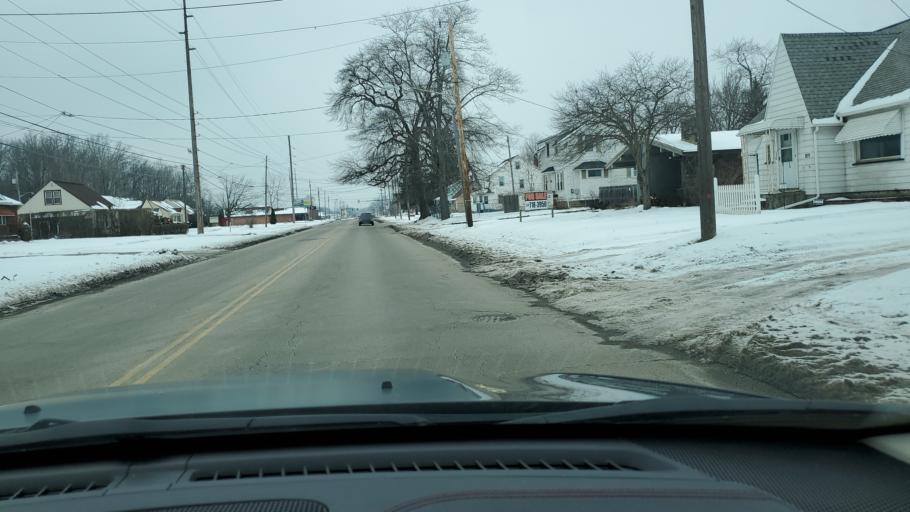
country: US
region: Ohio
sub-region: Trumbull County
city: Leavittsburg
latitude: 41.2479
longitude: -80.8483
